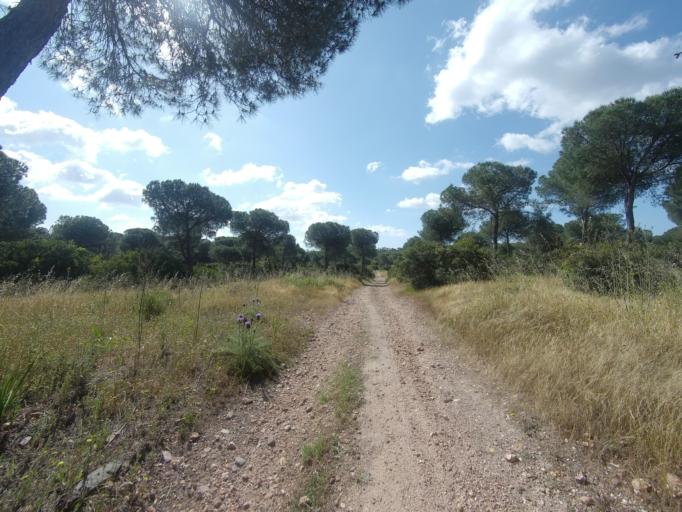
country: ES
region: Andalusia
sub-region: Provincia de Huelva
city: Aljaraque
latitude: 37.2401
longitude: -7.0293
